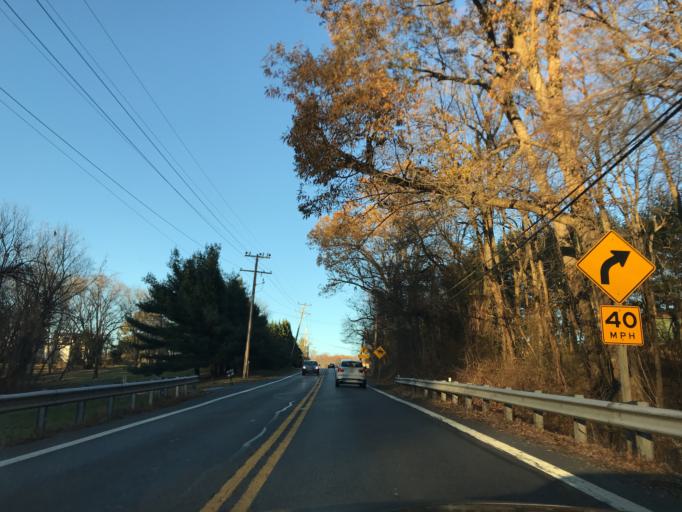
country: US
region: Maryland
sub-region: Howard County
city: Highland
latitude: 39.1684
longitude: -76.9677
